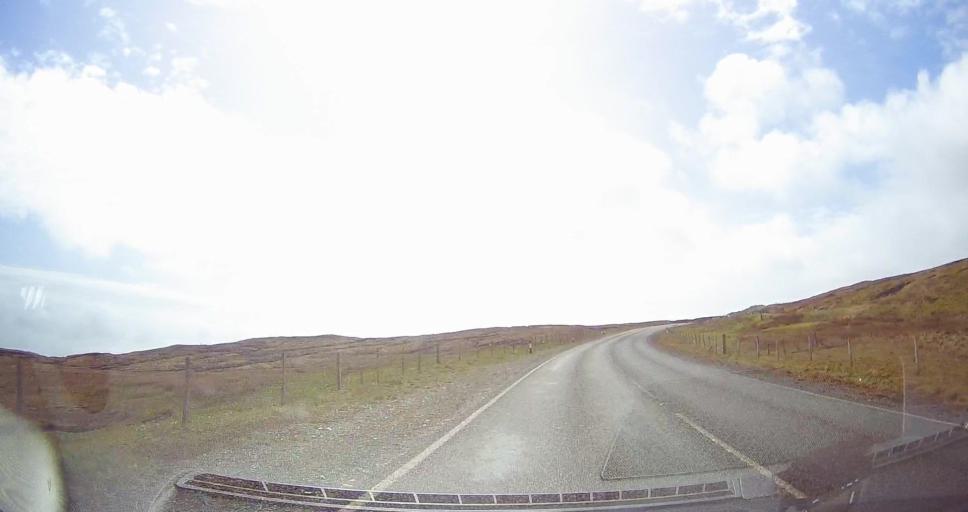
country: GB
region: Scotland
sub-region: Shetland Islands
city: Sandwick
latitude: 60.0922
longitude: -1.2287
